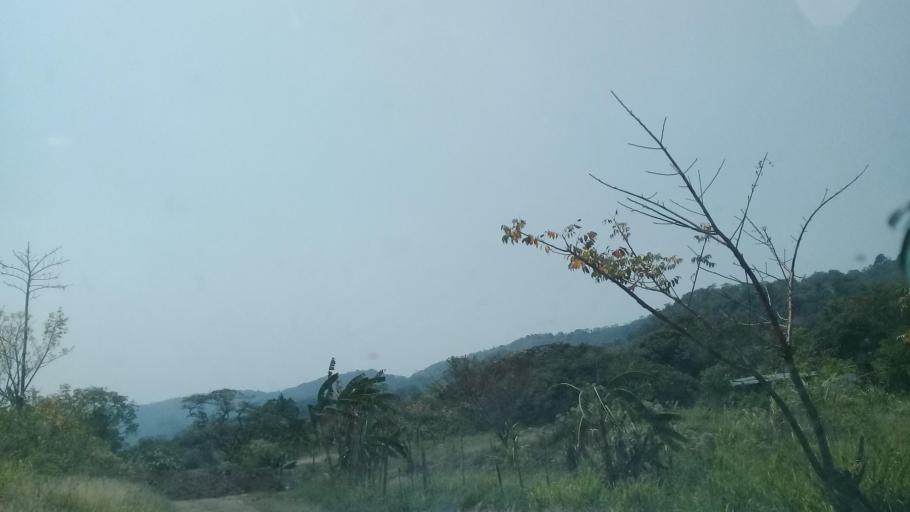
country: MX
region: Veracruz
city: El Castillo
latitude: 19.5642
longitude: -96.8418
